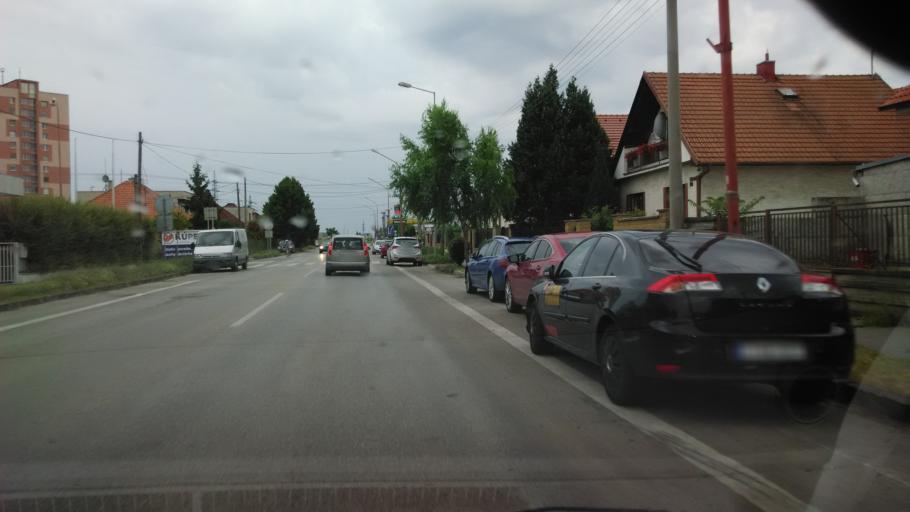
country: SK
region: Trnavsky
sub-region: Okres Trnava
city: Trnava
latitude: 48.3597
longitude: 17.5786
